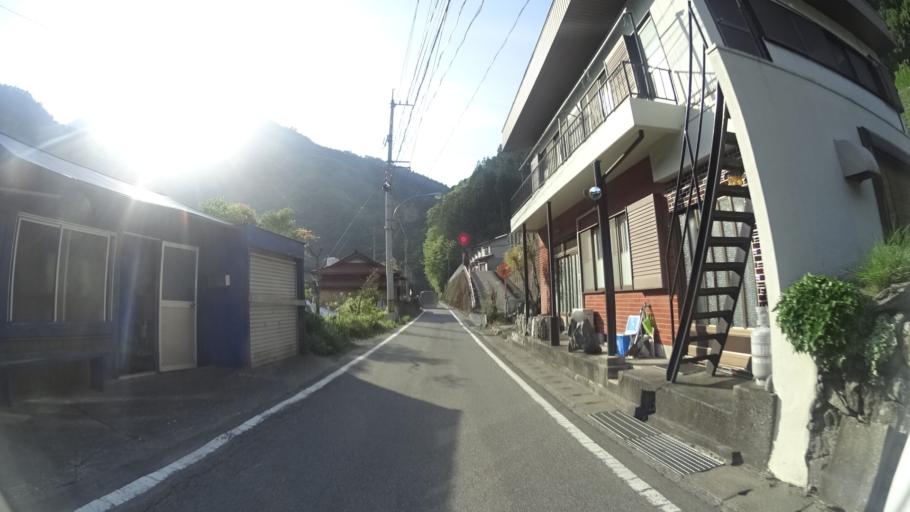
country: JP
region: Tokushima
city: Ikedacho
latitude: 33.8711
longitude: 133.8724
